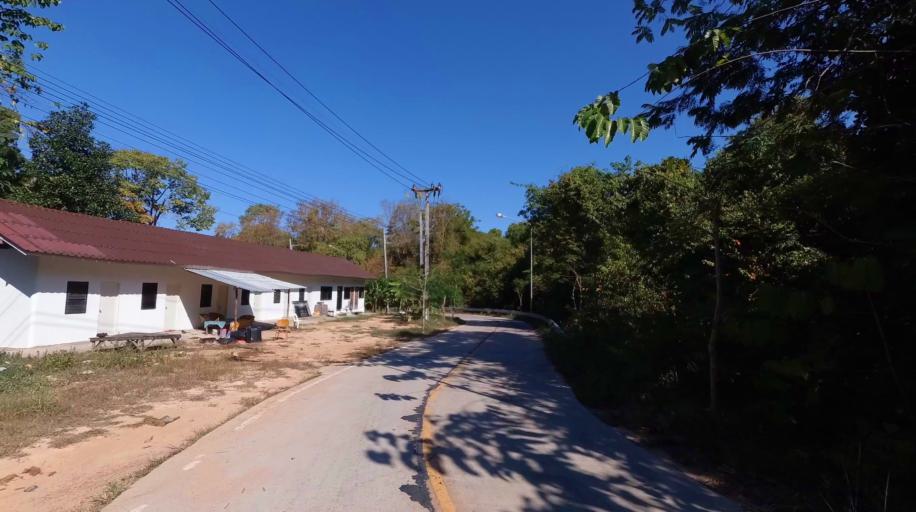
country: TH
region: Trat
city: Ko Kut
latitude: 11.6170
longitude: 102.5391
